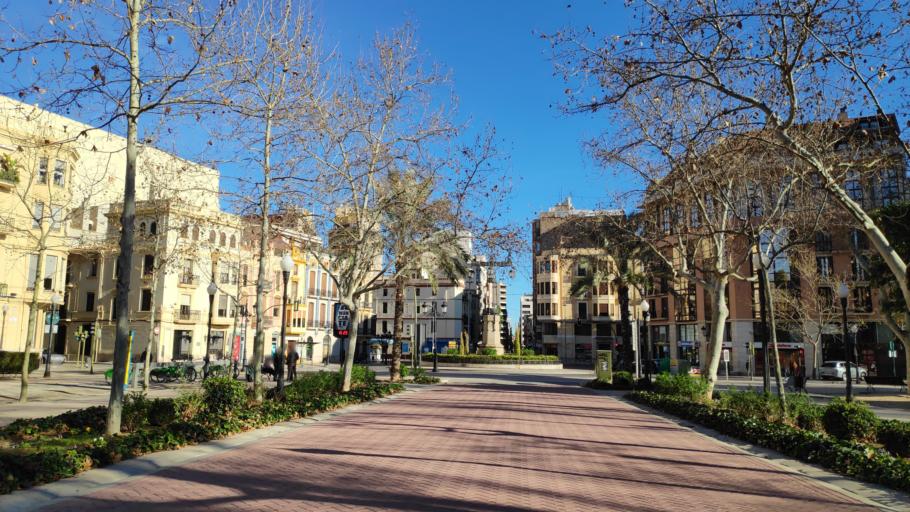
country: ES
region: Valencia
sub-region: Provincia de Castello
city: Castello de la Plana
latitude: 39.9879
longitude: -0.0435
